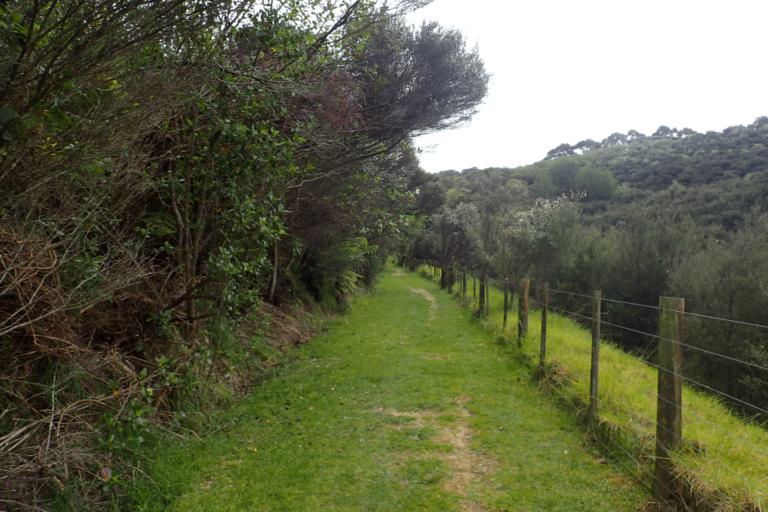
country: NZ
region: Auckland
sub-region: Auckland
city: Pakuranga
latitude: -36.7856
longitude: 174.9992
